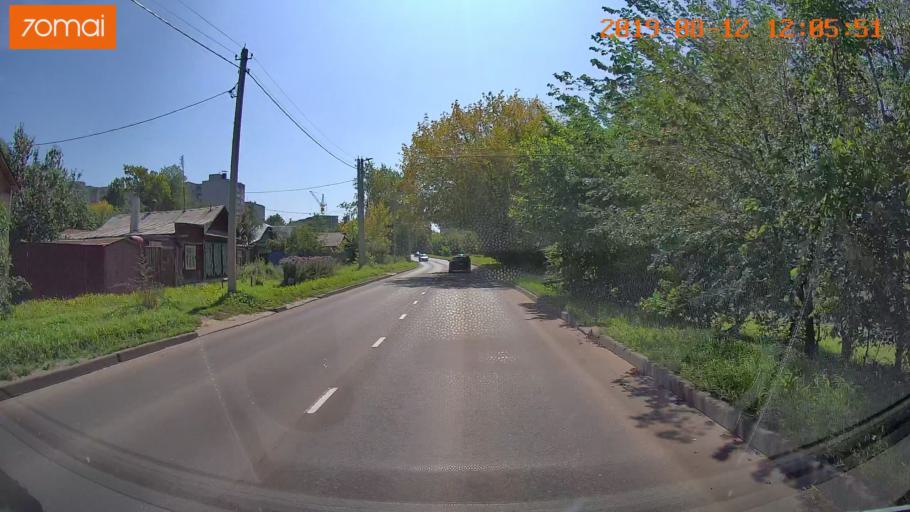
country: RU
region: Ivanovo
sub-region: Gorod Ivanovo
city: Ivanovo
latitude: 56.9918
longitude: 41.0189
